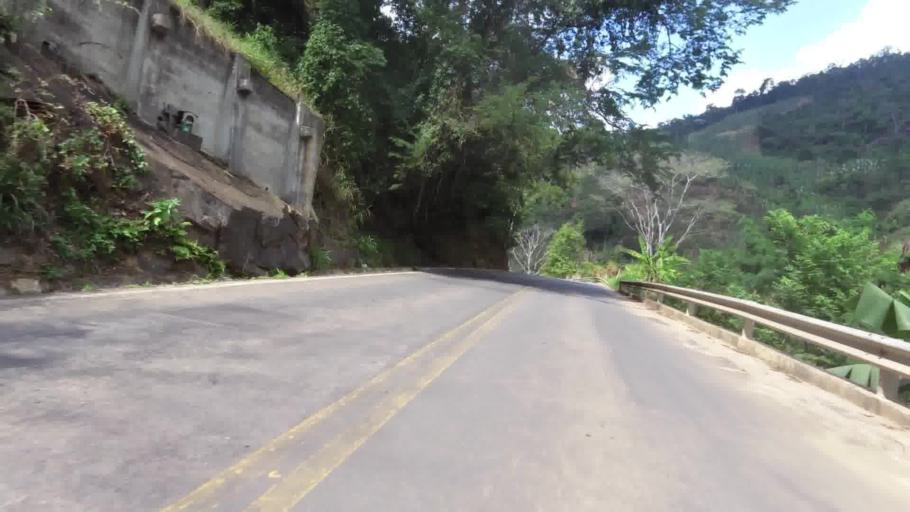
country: BR
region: Espirito Santo
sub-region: Alfredo Chaves
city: Alfredo Chaves
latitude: -20.6239
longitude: -40.7767
